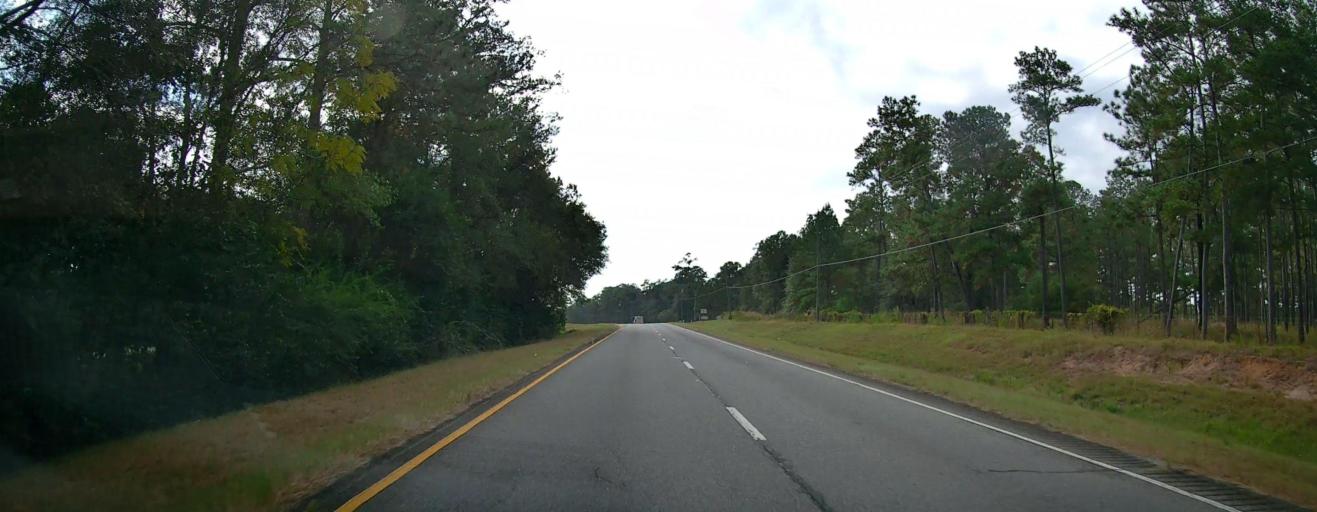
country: US
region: Georgia
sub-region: Thomas County
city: Thomasville
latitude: 30.7710
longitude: -84.0765
